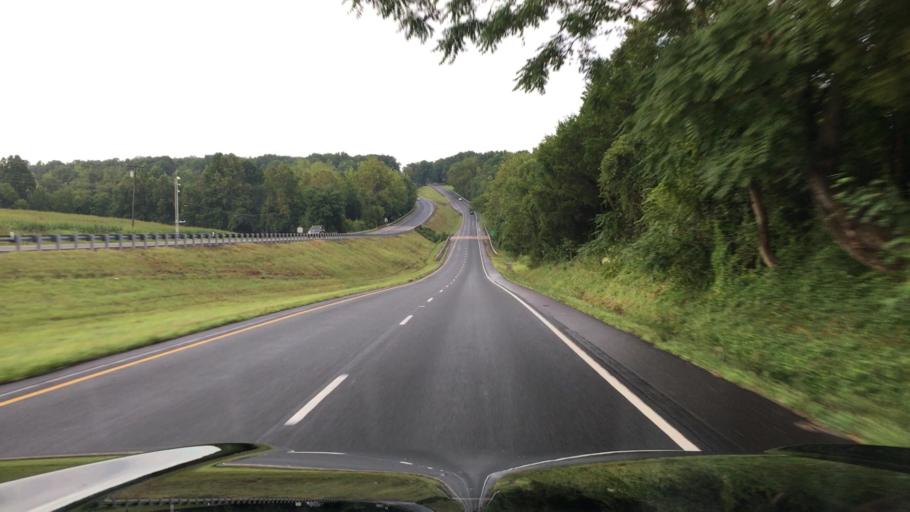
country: US
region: Virginia
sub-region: Culpeper County
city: Merrimac
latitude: 38.4417
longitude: -78.1335
